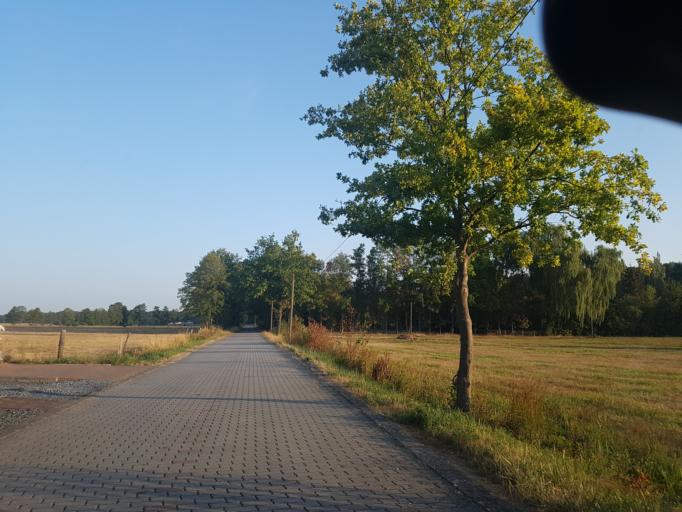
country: DE
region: Brandenburg
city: Falkenberg
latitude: 51.6412
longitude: 13.2962
